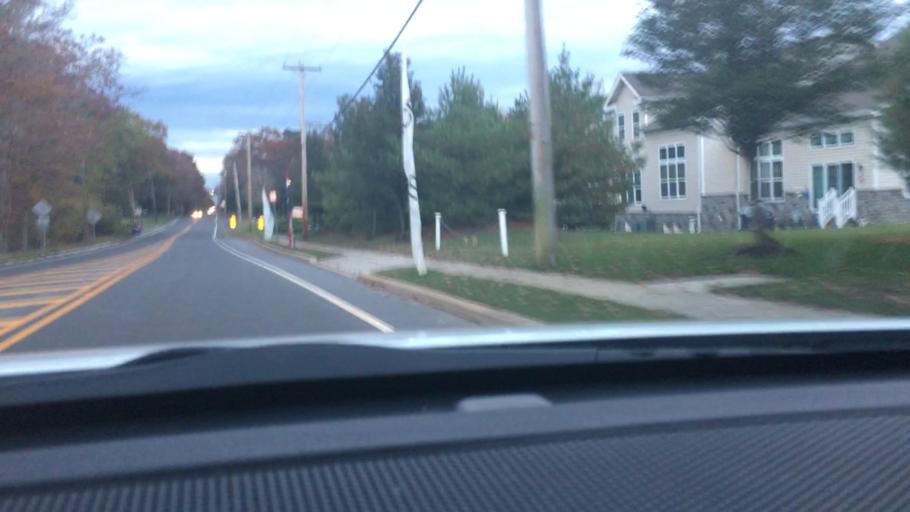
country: US
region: New Jersey
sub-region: Atlantic County
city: Absecon
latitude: 39.4403
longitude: -74.4979
